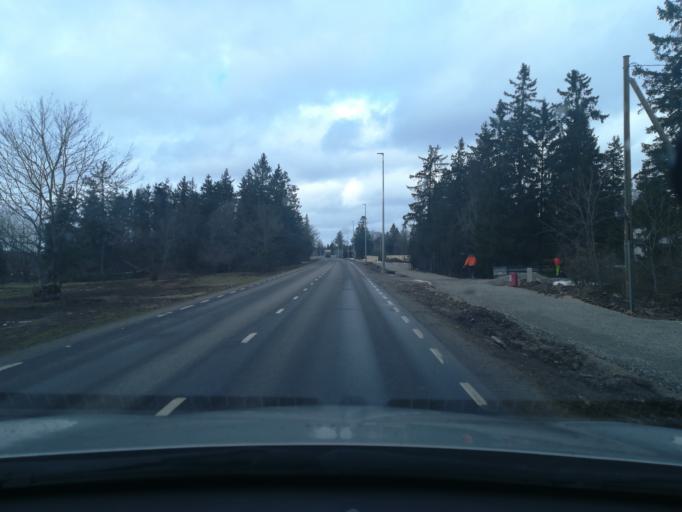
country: EE
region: Harju
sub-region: Harku vald
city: Tabasalu
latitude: 59.4271
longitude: 24.5271
